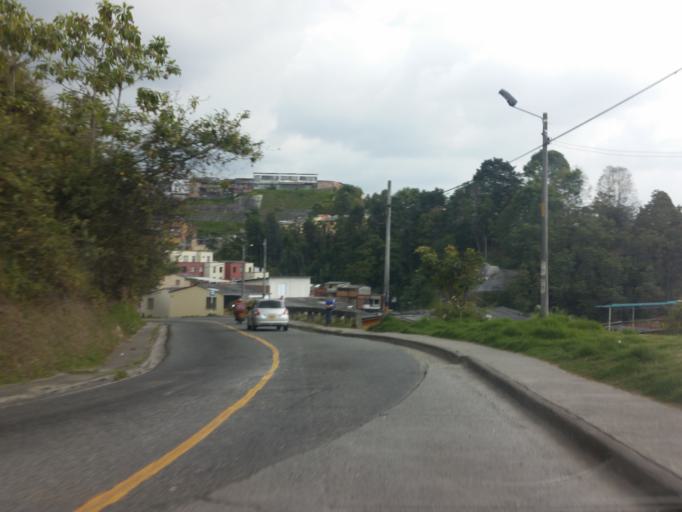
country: CO
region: Caldas
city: Manizales
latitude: 5.0631
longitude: -75.5068
